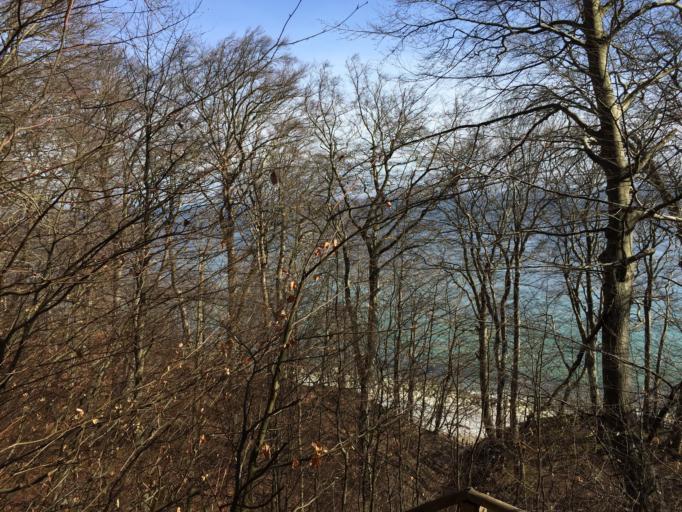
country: DE
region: Mecklenburg-Vorpommern
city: Sassnitz
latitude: 54.5247
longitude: 13.6694
